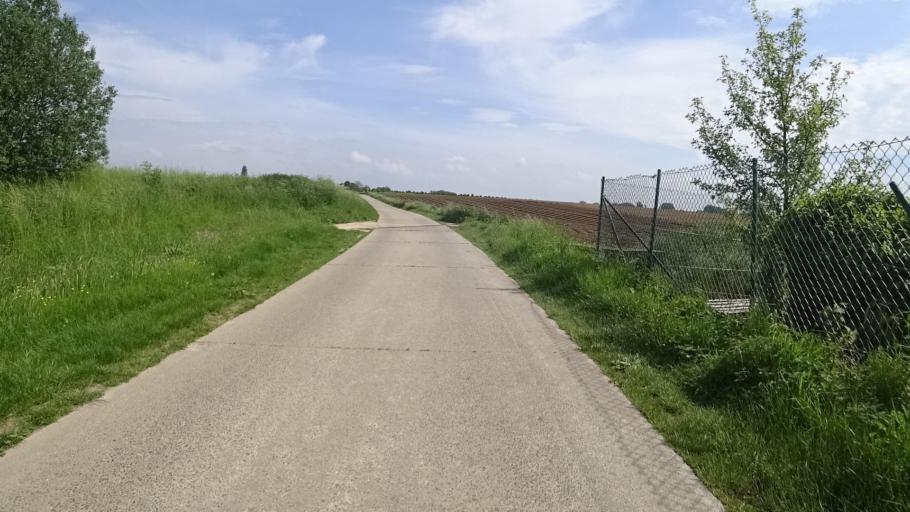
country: BE
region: Wallonia
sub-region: Province du Brabant Wallon
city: Walhain-Saint-Paul
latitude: 50.6482
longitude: 4.6622
